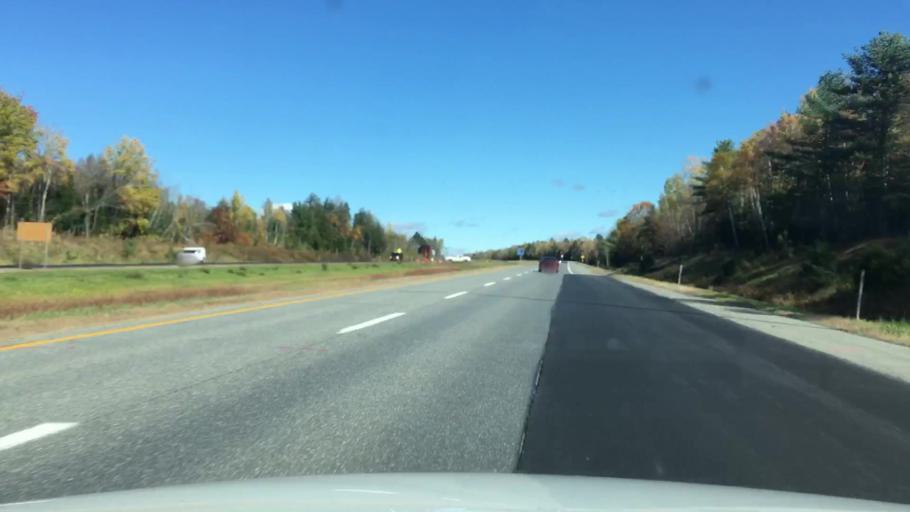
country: US
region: Maine
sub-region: Penobscot County
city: Medway
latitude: 45.6102
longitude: -68.5176
